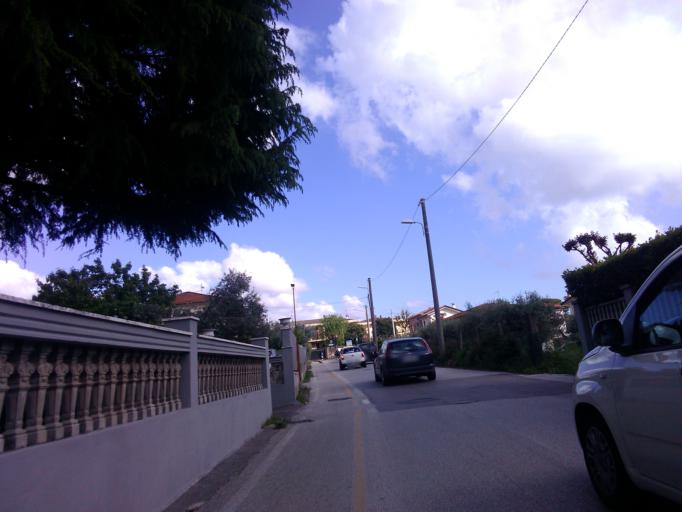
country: IT
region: Tuscany
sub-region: Provincia di Massa-Carrara
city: Massa
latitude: 44.0218
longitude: 10.1231
